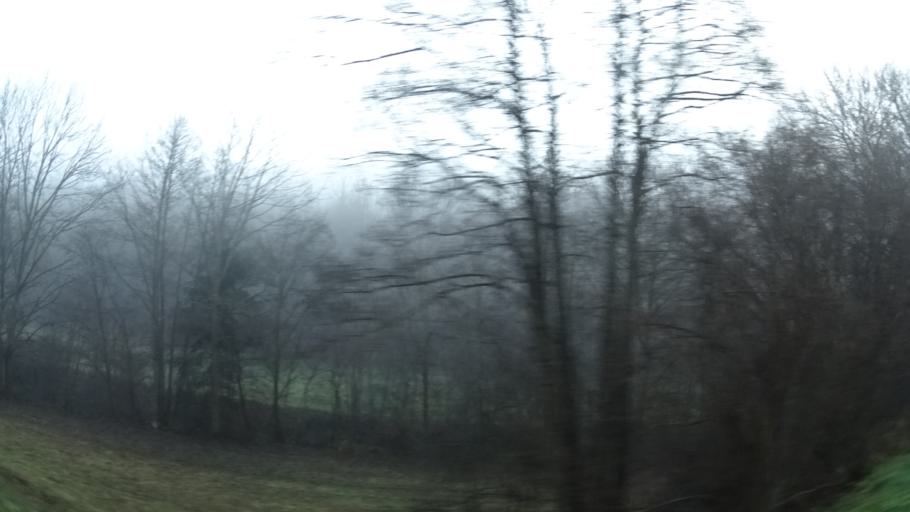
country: DE
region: Bavaria
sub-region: Regierungsbezirk Unterfranken
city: Neunkirchen
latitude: 49.6678
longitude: 9.3727
